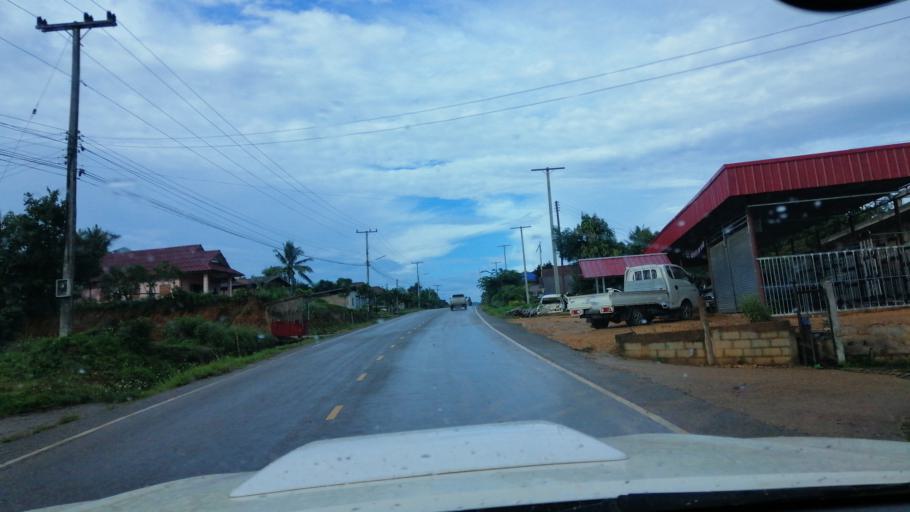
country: TH
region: Nan
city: Thung Chang
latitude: 19.6364
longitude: 100.8145
